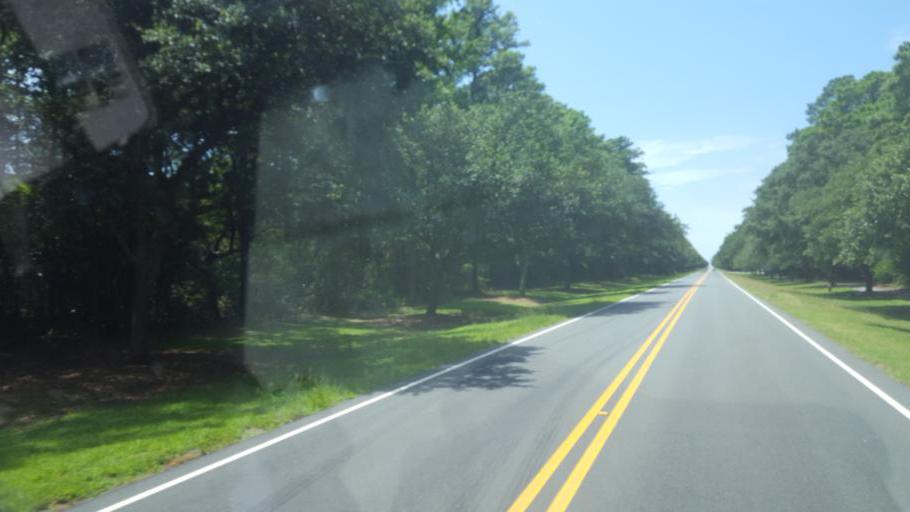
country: US
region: North Carolina
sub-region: Dare County
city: Manteo
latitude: 35.9313
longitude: -75.7116
